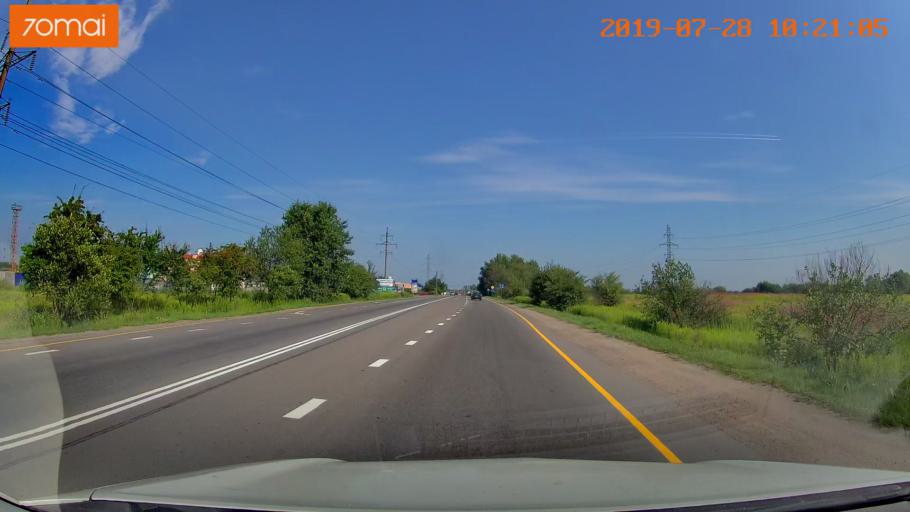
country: RU
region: Kaliningrad
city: Maloye Isakovo
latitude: 54.7541
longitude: 20.5654
